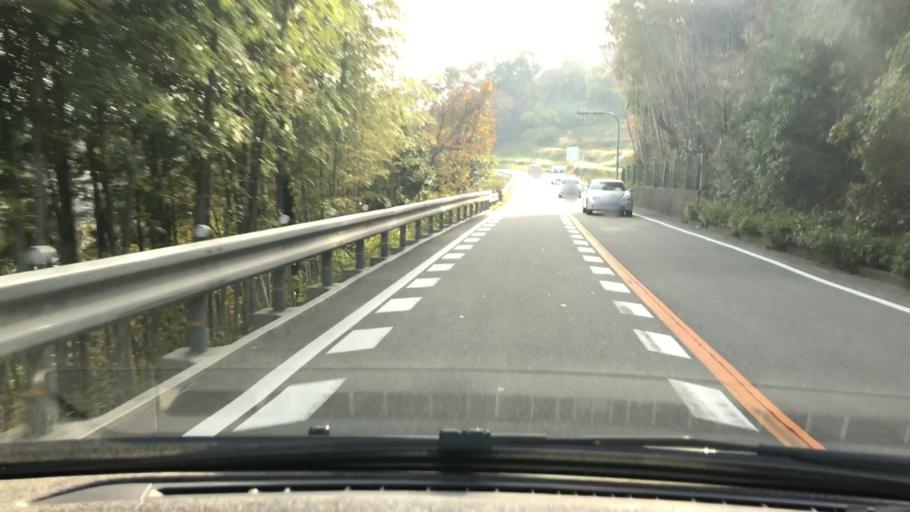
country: JP
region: Hyogo
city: Sandacho
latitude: 34.8338
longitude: 135.2743
